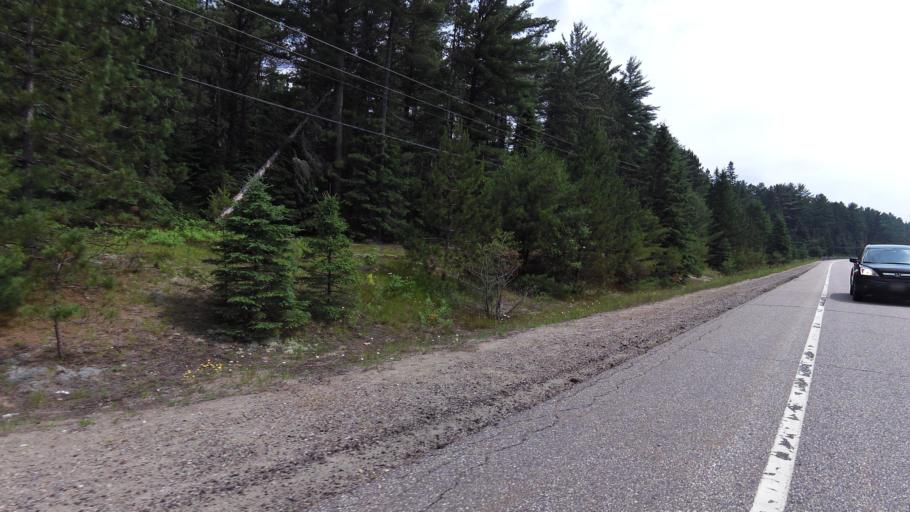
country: CA
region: Ontario
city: Huntsville
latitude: 45.5798
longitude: -78.5110
